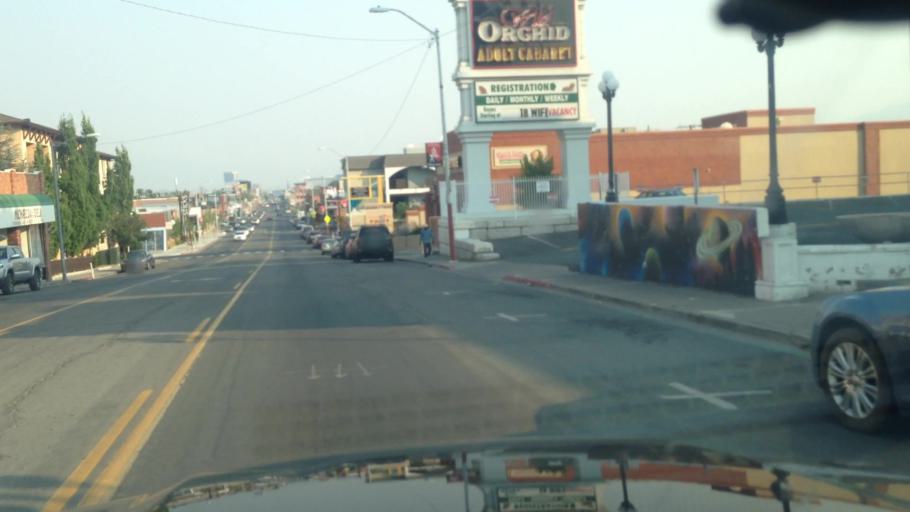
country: US
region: Nevada
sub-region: Washoe County
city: Reno
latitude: 39.5198
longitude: -119.8101
